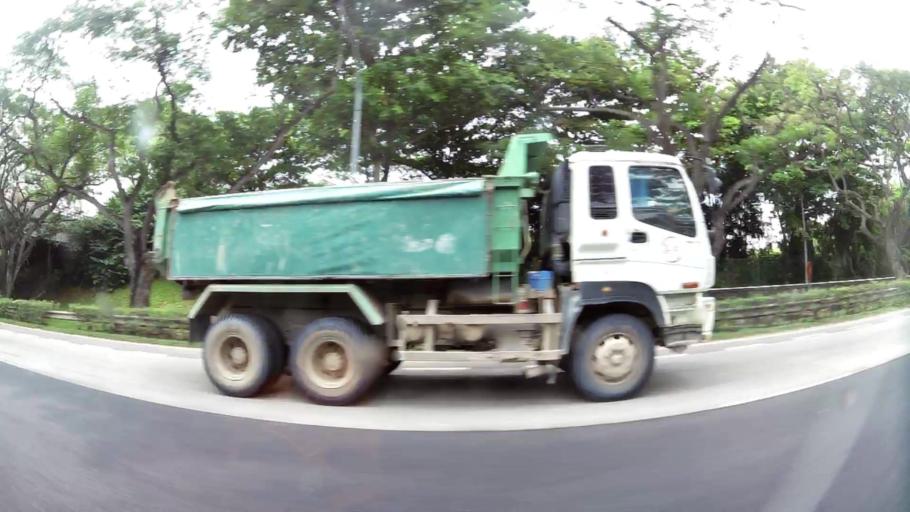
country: SG
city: Singapore
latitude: 1.3267
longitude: 103.9730
